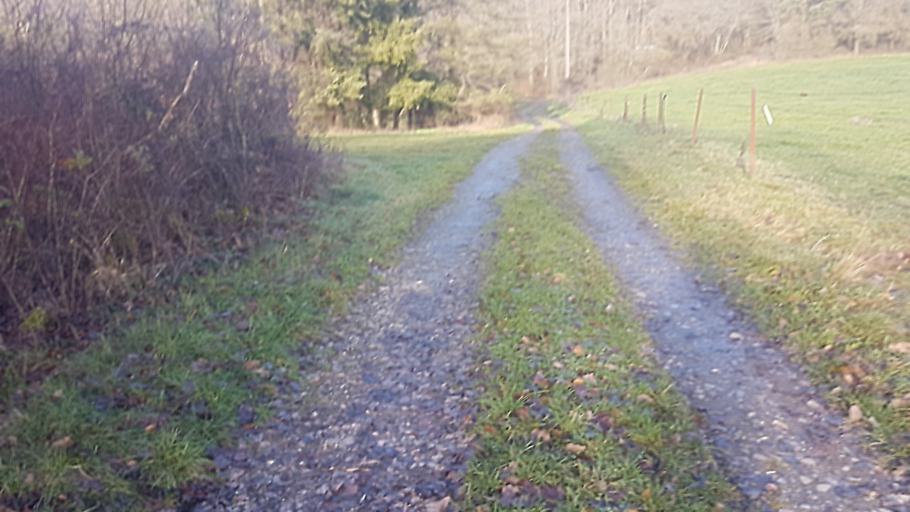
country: FR
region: Champagne-Ardenne
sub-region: Departement des Ardennes
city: Vireux-Molhain
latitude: 50.0762
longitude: 4.6187
